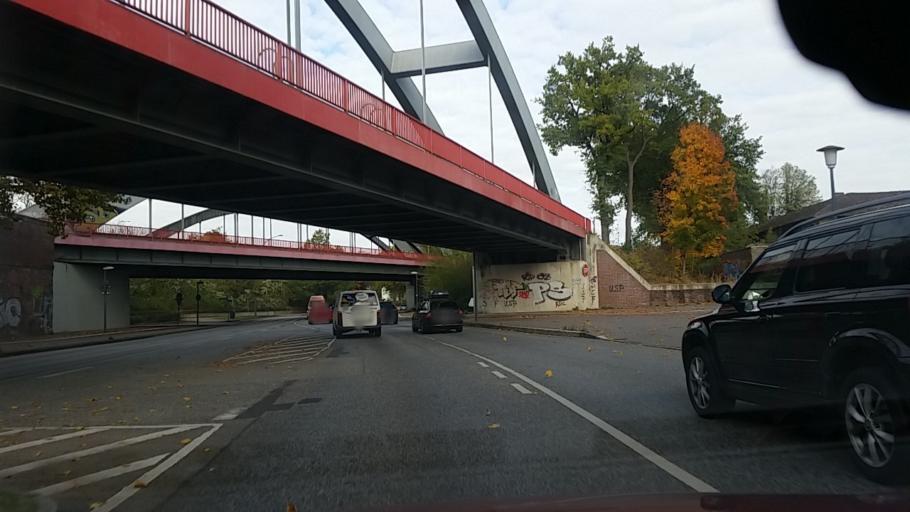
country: DE
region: Hamburg
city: Ohlsdorf
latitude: 53.6231
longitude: 10.0328
